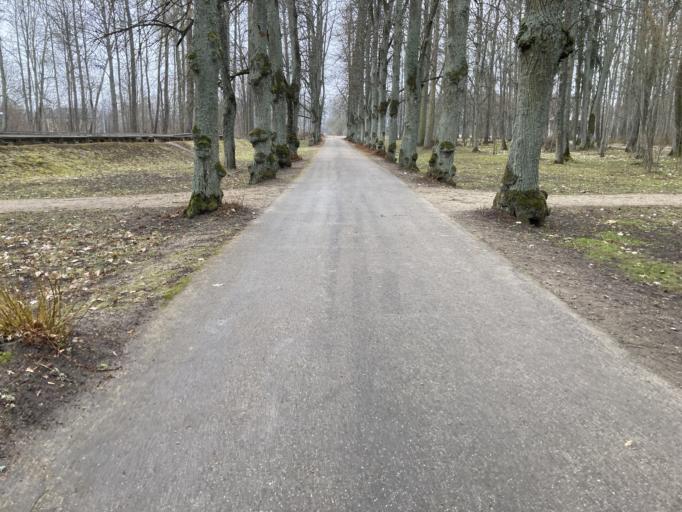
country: LT
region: Siauliu apskritis
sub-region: Joniskis
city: Joniskis
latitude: 56.4250
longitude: 23.7004
